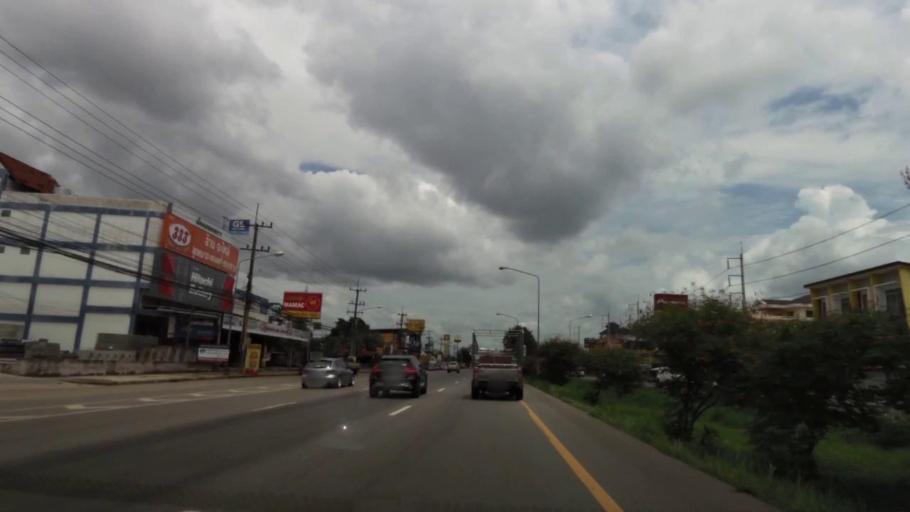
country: TH
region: Rayong
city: Klaeng
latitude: 12.7866
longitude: 101.6673
